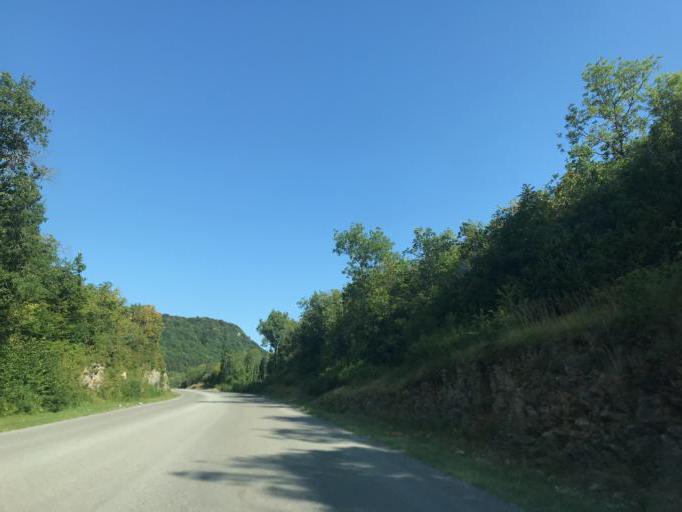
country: FR
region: Franche-Comte
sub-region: Departement du Jura
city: Lavans-les-Saint-Claude
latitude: 46.3824
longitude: 5.7506
